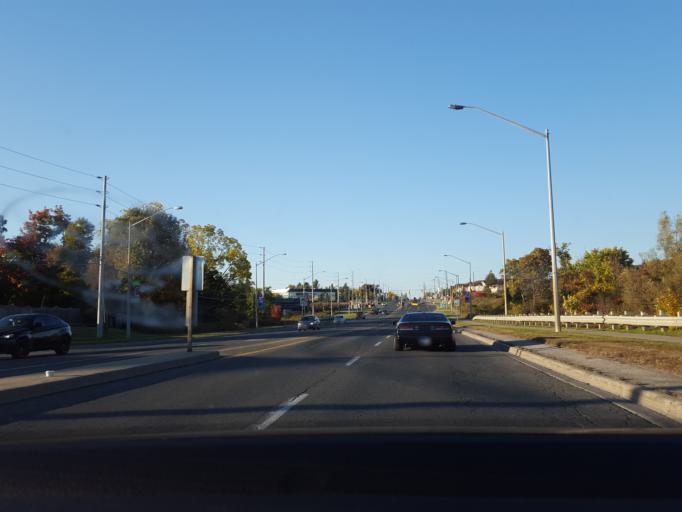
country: CA
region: Ontario
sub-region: York
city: Richmond Hill
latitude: 43.9050
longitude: -79.4450
